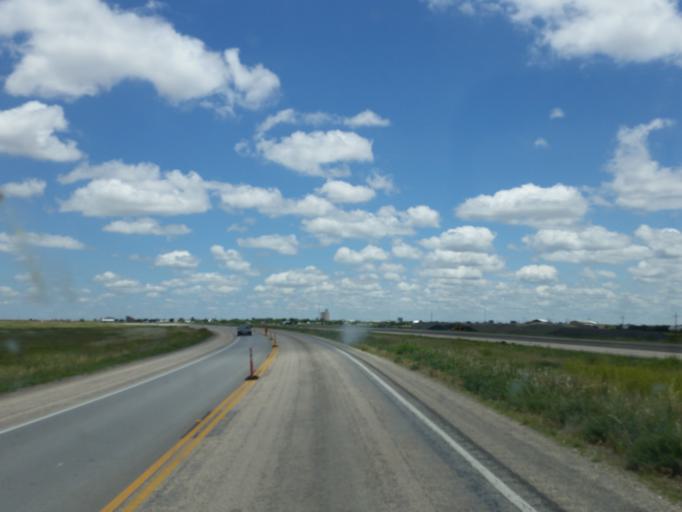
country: US
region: Texas
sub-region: Nolan County
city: Roscoe
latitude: 32.4535
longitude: -100.5553
